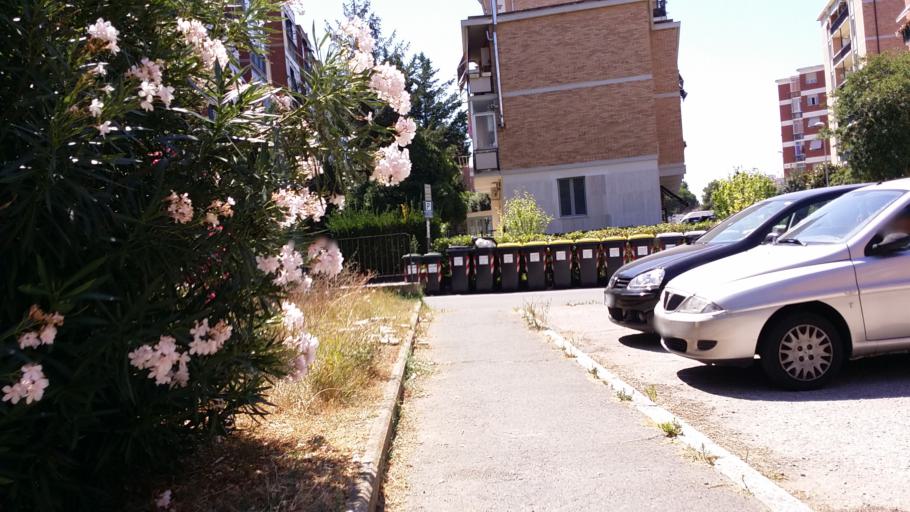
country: IT
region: Tuscany
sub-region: Provincia di Livorno
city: Livorno
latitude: 43.5447
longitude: 10.3309
